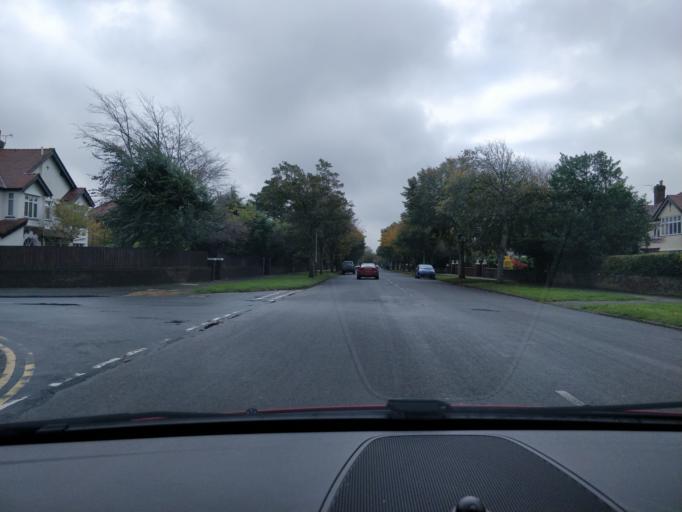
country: GB
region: England
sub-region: Sefton
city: Southport
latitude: 53.6180
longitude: -3.0218
